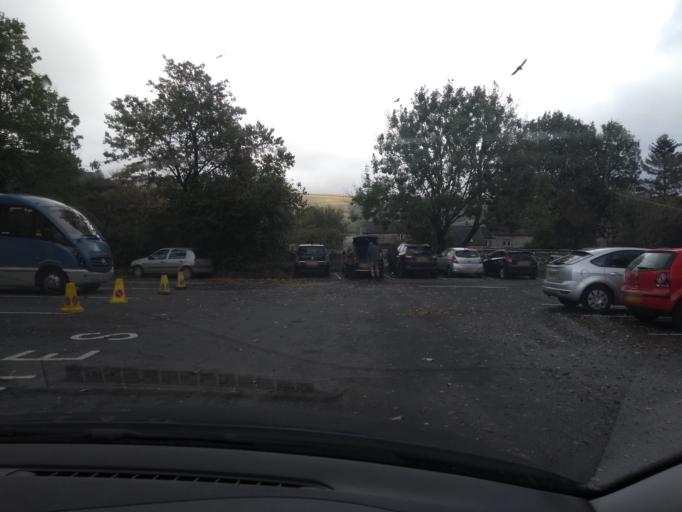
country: GB
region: England
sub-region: North Yorkshire
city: Gargrave
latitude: 54.0605
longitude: -2.1546
